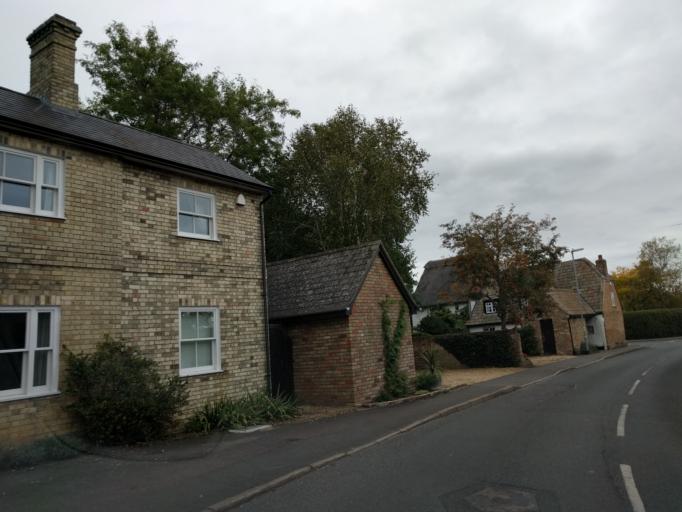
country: GB
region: England
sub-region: Cambridgeshire
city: Earith
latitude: 52.3548
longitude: 0.0077
